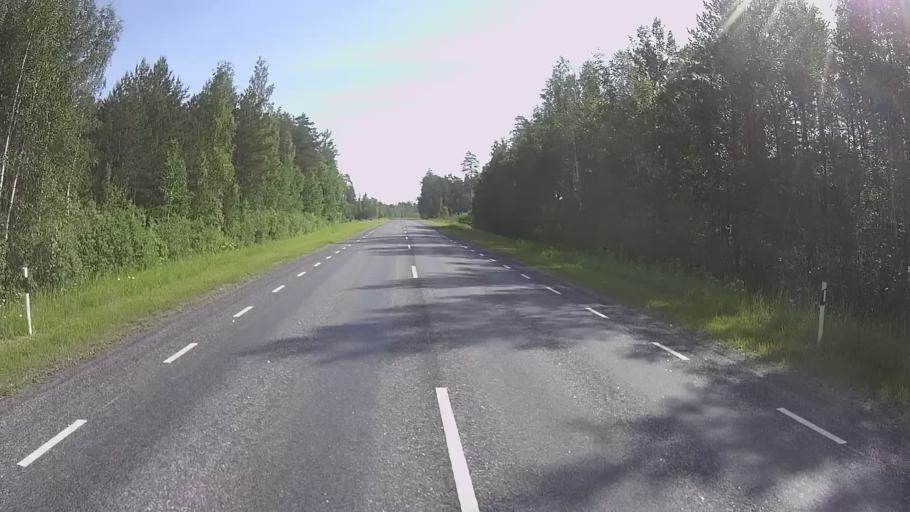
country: EE
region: Valgamaa
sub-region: Torva linn
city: Torva
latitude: 58.0526
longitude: 25.9972
